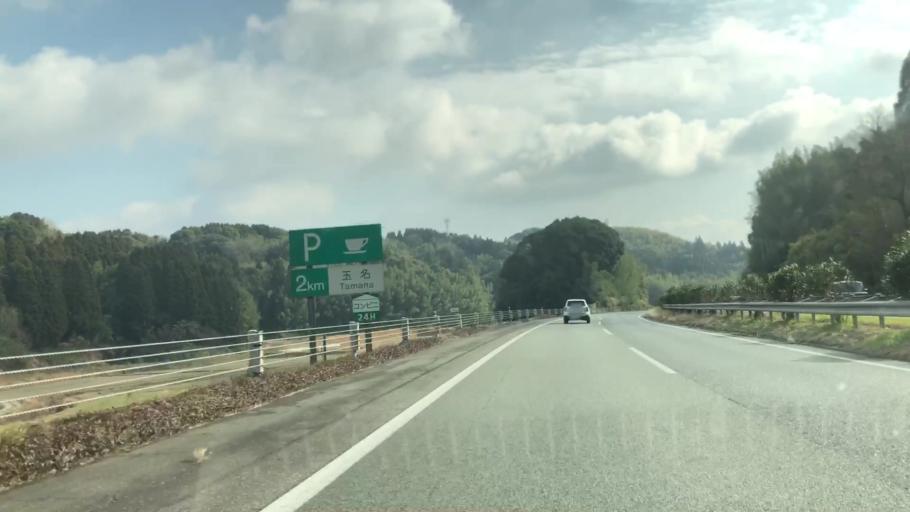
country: JP
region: Kumamoto
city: Yamaga
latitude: 33.0292
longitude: 130.5757
